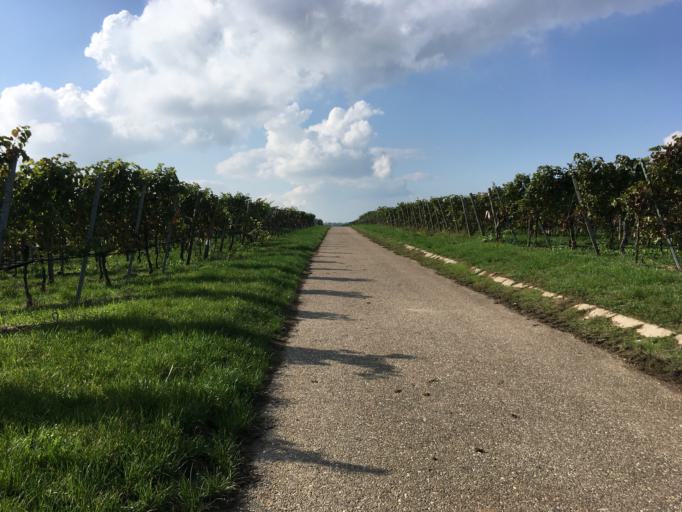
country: DE
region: Baden-Wuerttemberg
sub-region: Regierungsbezirk Stuttgart
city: Kirchheim am Neckar
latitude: 49.0561
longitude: 9.1608
